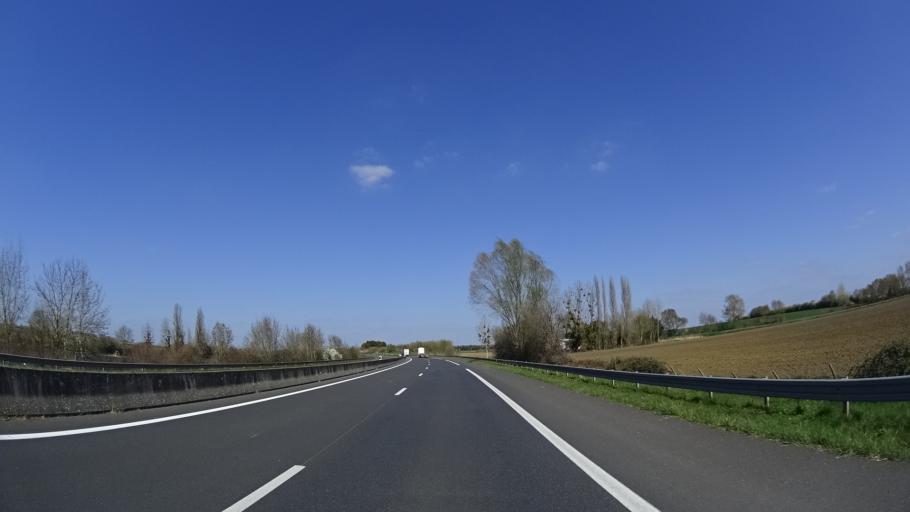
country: FR
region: Pays de la Loire
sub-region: Departement de Maine-et-Loire
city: Saint-Jean
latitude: 47.2427
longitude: -0.3211
